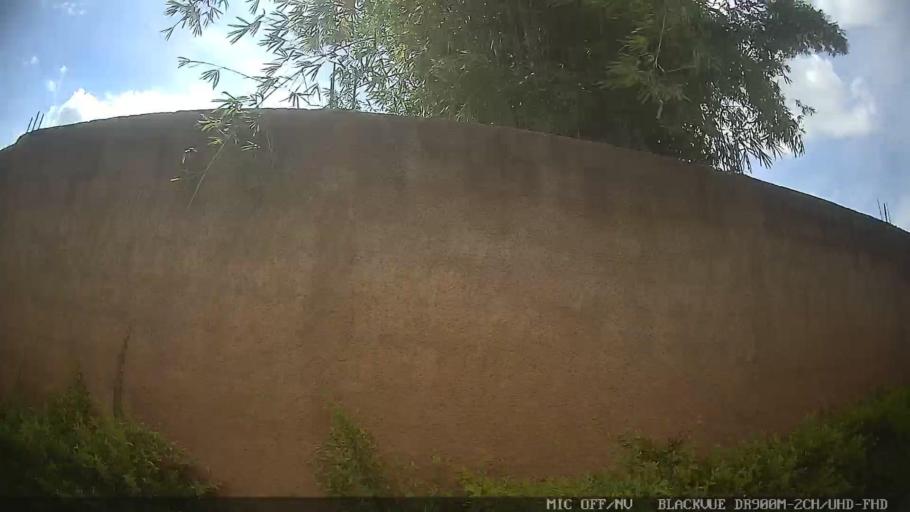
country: BR
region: Sao Paulo
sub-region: Atibaia
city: Atibaia
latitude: -23.0915
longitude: -46.5453
